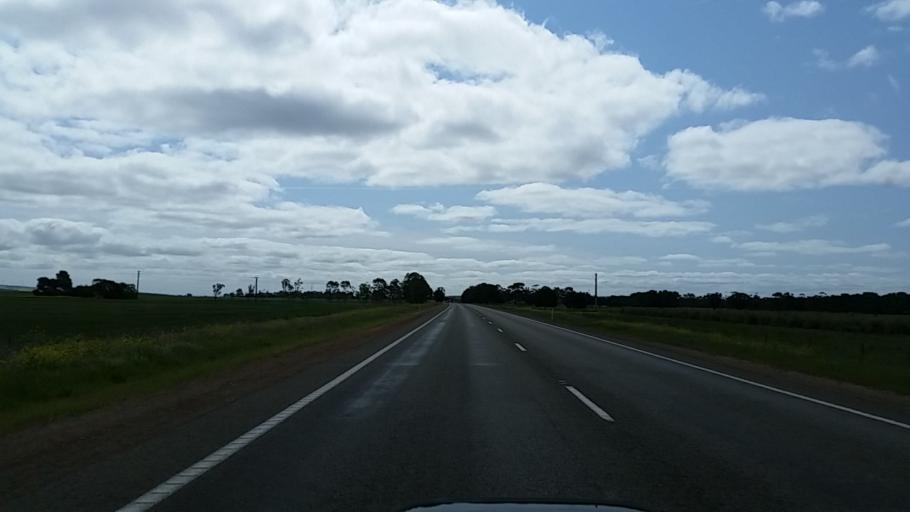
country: AU
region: South Australia
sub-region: Port Pirie City and Dists
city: Crystal Brook
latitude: -33.5468
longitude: 138.2191
